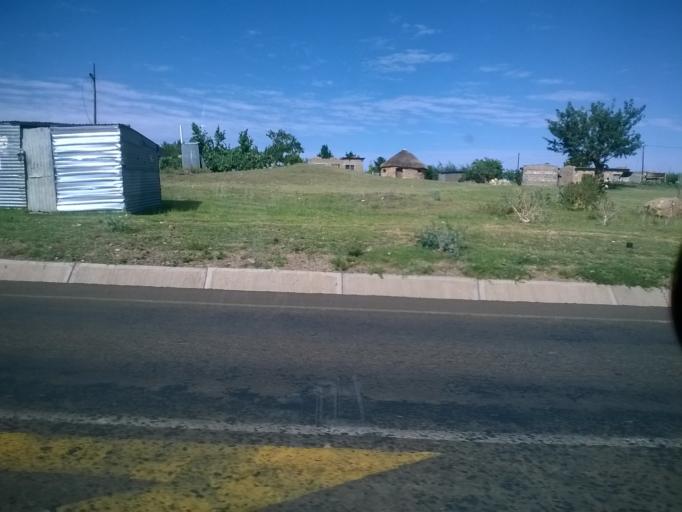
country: LS
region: Berea
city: Teyateyaneng
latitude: -29.1006
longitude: 27.9592
